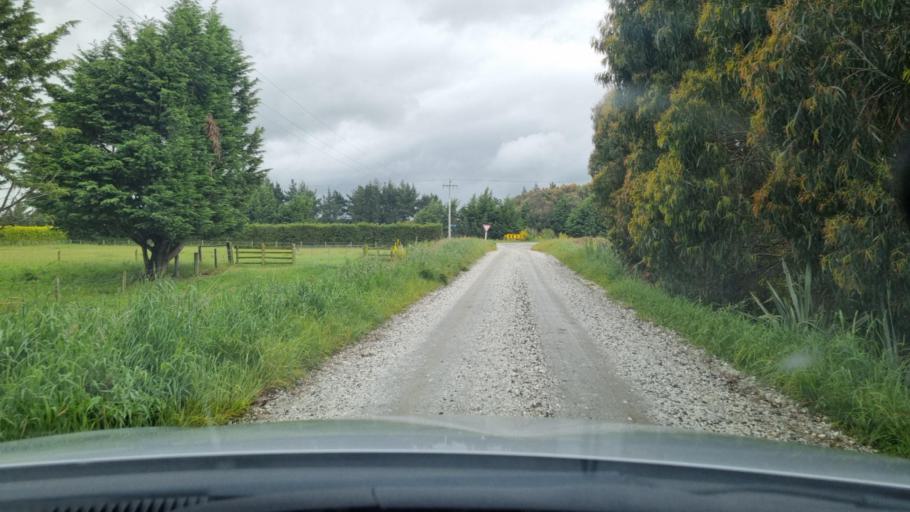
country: NZ
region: Southland
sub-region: Invercargill City
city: Invercargill
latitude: -46.4517
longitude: 168.3883
